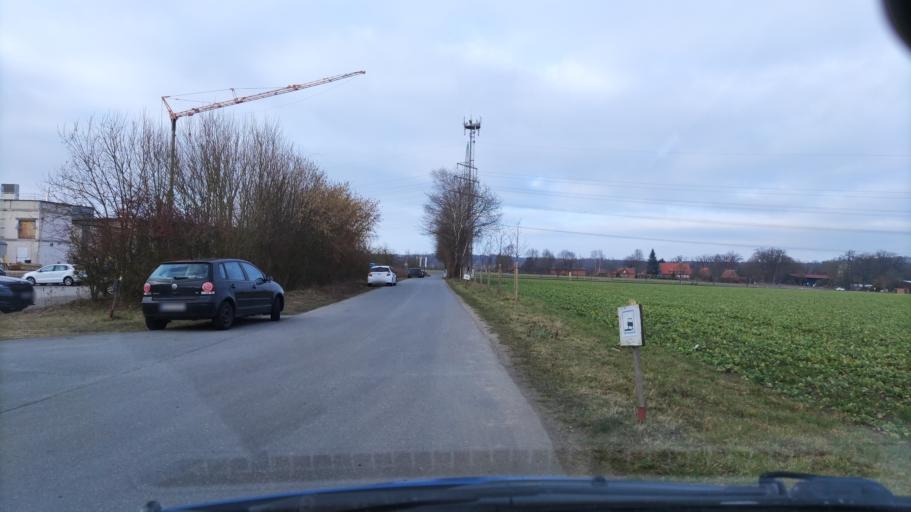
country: DE
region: Lower Saxony
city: Gerdau
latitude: 52.9578
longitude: 10.4522
